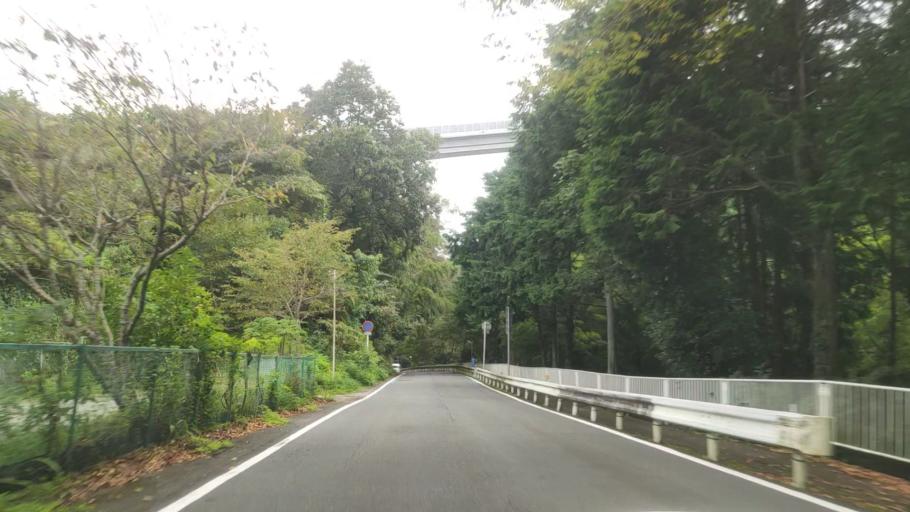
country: JP
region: Wakayama
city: Hashimoto
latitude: 34.2847
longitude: 135.5608
